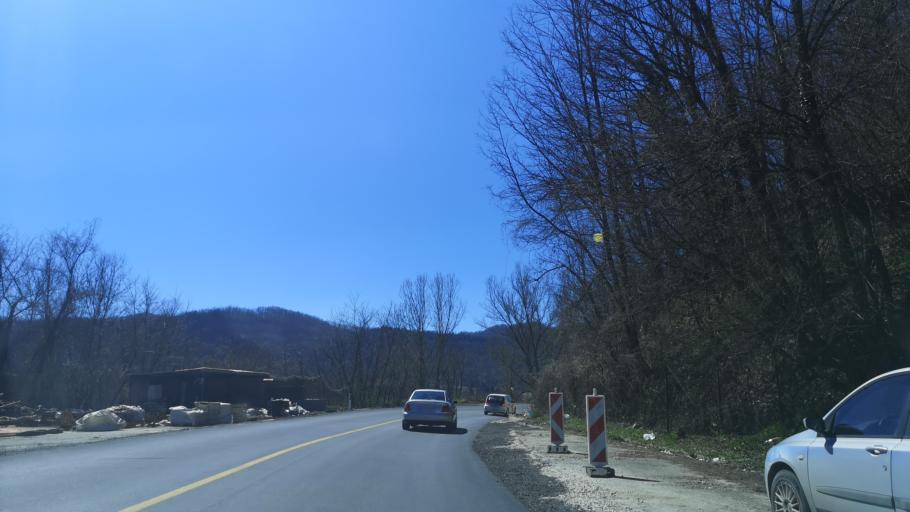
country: RS
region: Central Serbia
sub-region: Moravicki Okrug
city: Lucani
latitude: 43.8711
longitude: 20.1166
